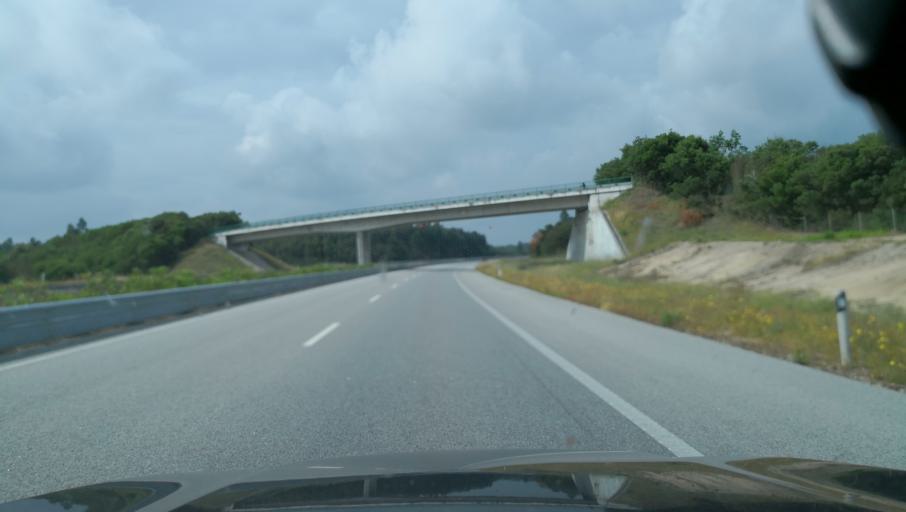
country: PT
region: Coimbra
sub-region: Montemor-O-Velho
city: Arazede
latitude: 40.2929
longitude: -8.7420
